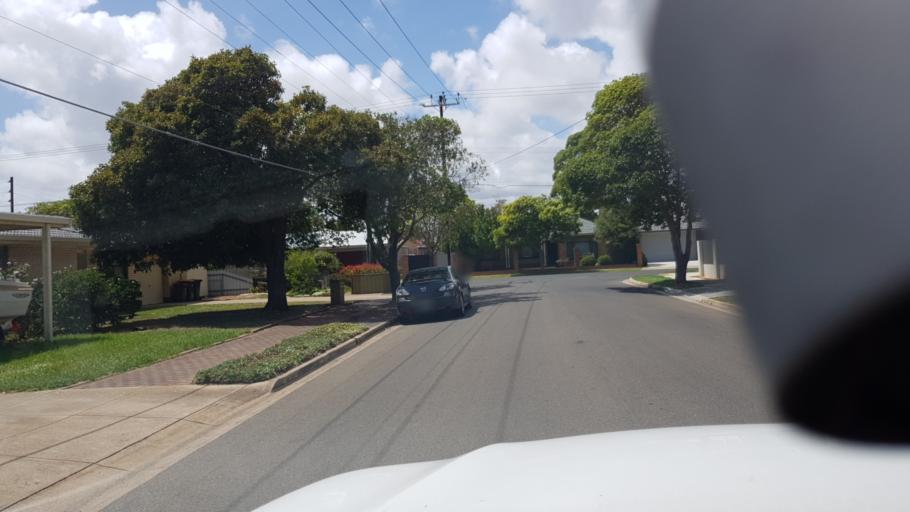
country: AU
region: South Australia
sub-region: Holdfast Bay
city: North Brighton
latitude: -35.0057
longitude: 138.5304
